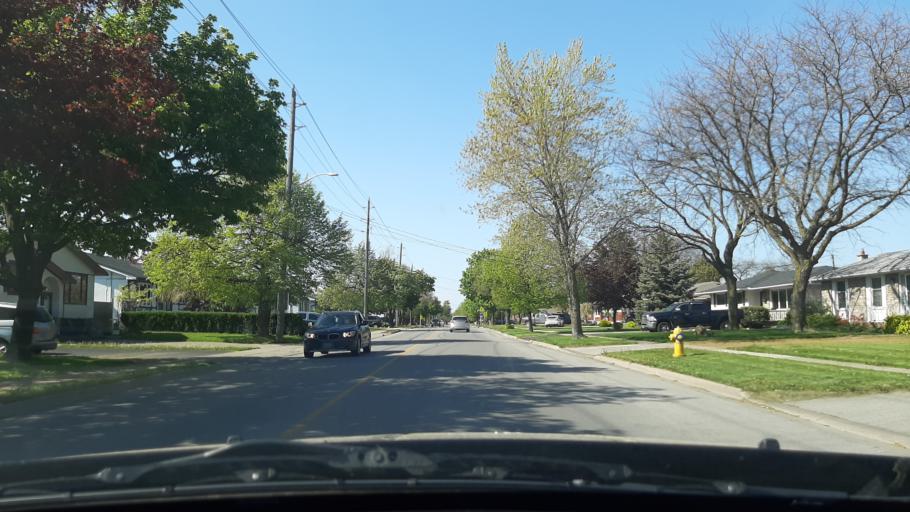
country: CA
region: Ontario
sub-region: Regional Municipality of Niagara
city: St. Catharines
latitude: 43.1962
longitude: -79.2112
